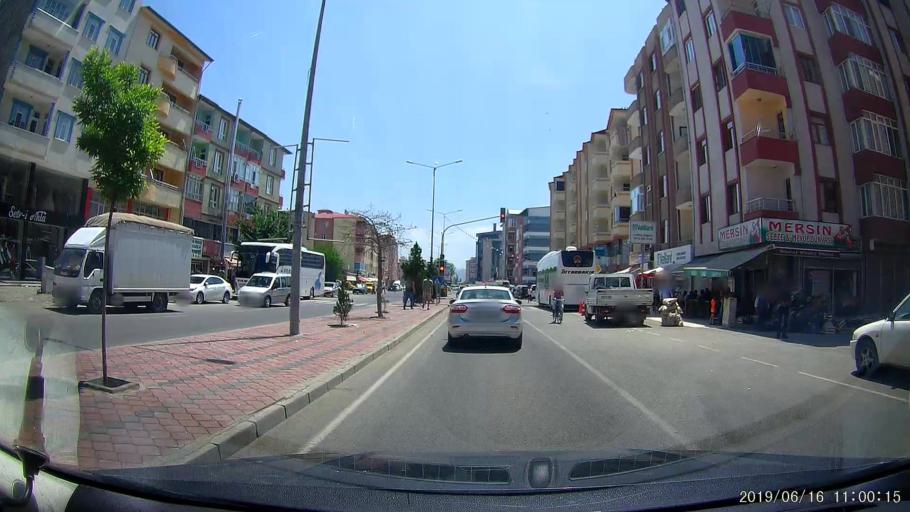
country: TR
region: Igdir
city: Igdir
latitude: 39.9189
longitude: 44.0425
